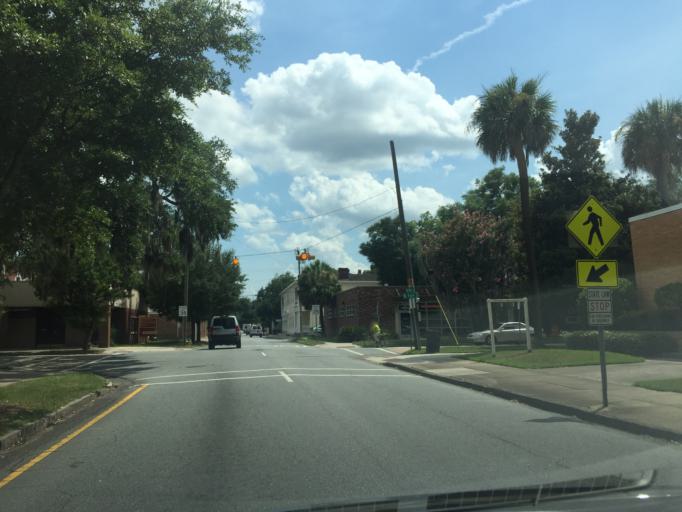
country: US
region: Georgia
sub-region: Chatham County
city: Savannah
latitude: 32.0655
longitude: -81.0982
